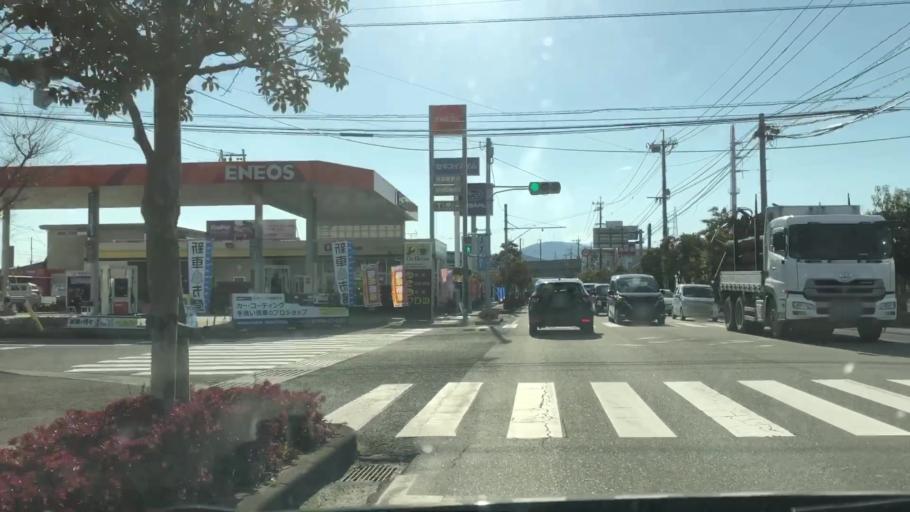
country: JP
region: Kagoshima
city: Satsumasendai
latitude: 31.8331
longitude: 130.3098
